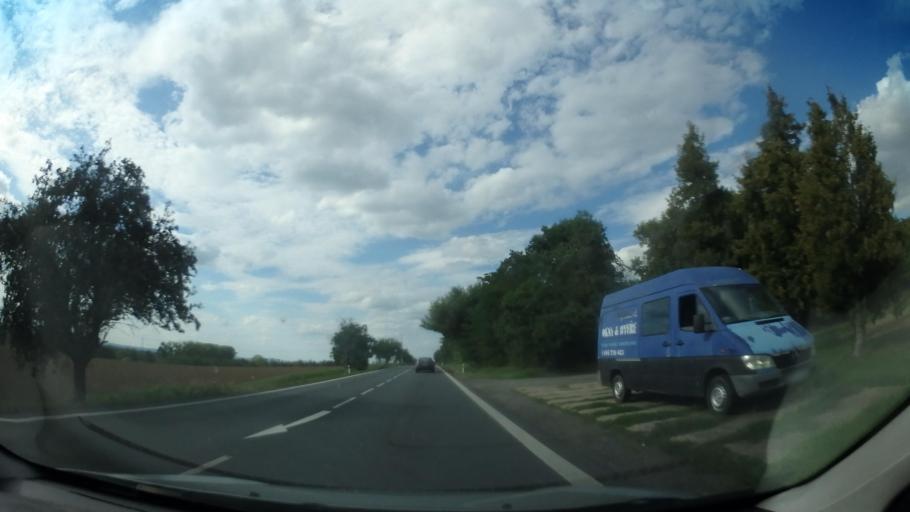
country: CZ
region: Central Bohemia
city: Zleby
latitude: 49.8726
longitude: 15.4341
